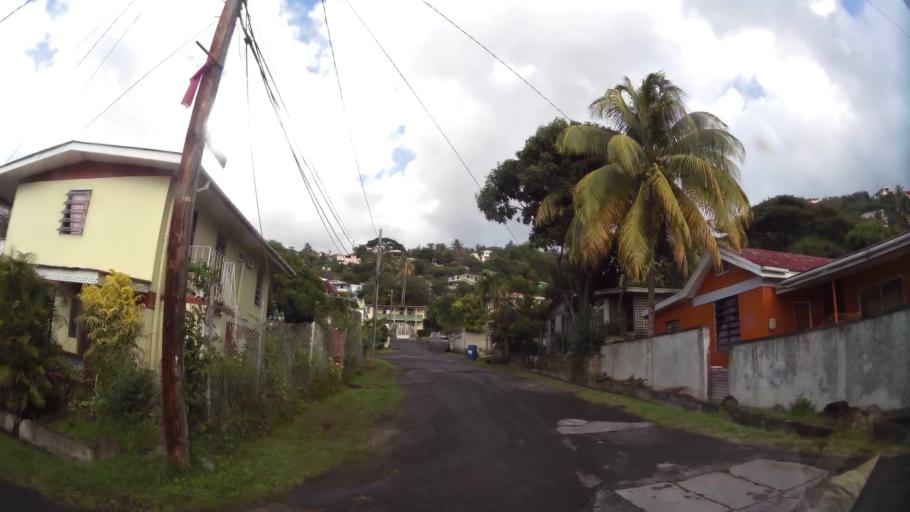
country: DM
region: Saint Paul
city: Mahaut
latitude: 15.3362
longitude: -61.3898
